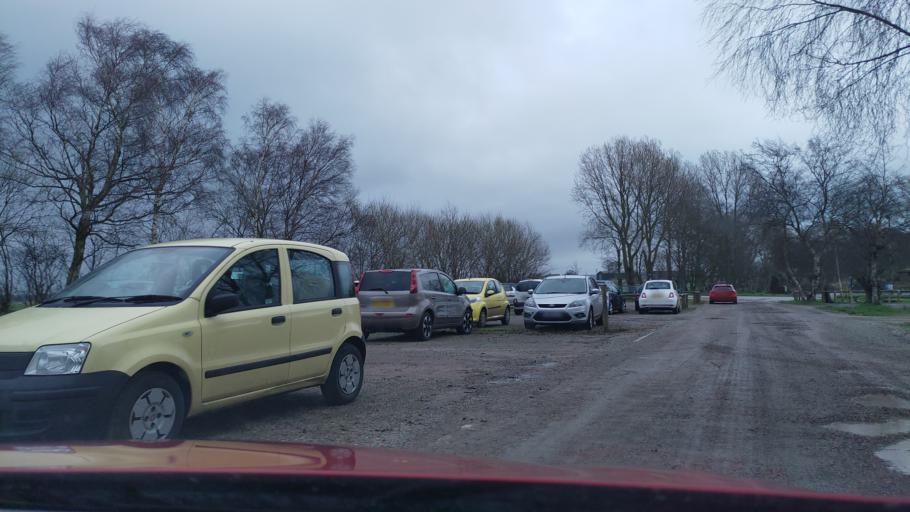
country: GB
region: England
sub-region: Lancashire
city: Ormskirk
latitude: 53.6233
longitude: -2.8654
